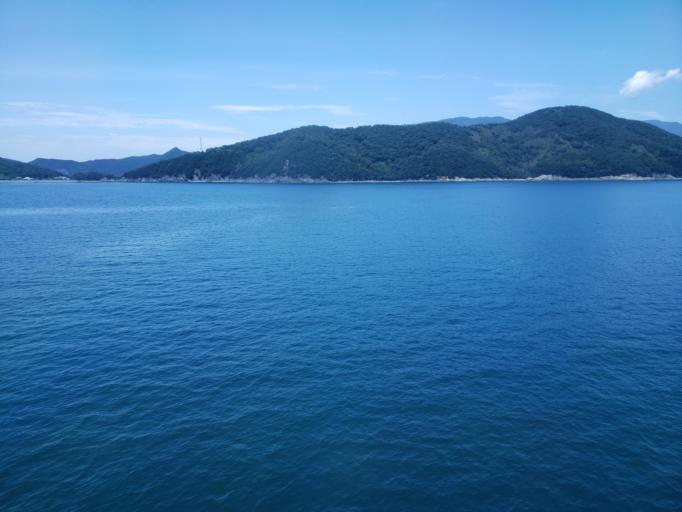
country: JP
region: Kagawa
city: Tonosho
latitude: 34.4402
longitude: 134.3000
